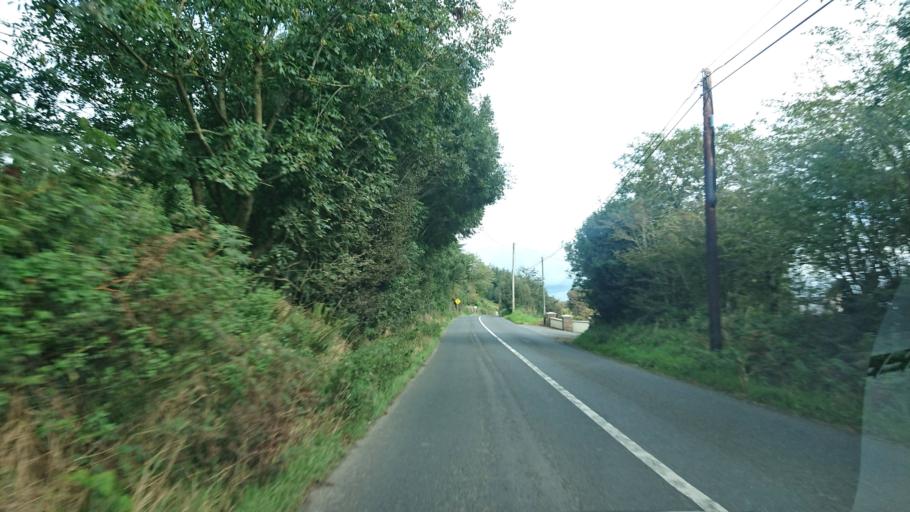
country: IE
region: Munster
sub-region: Waterford
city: Portlaw
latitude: 52.2630
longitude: -7.3264
